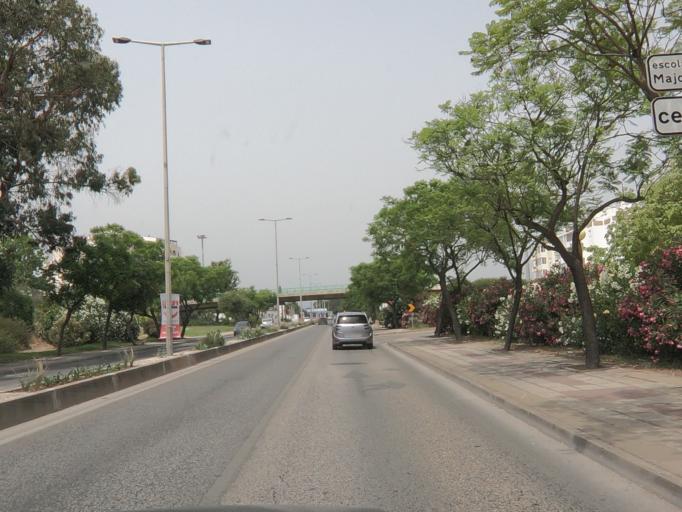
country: PT
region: Faro
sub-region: Portimao
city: Portimao
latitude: 37.1357
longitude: -8.5456
